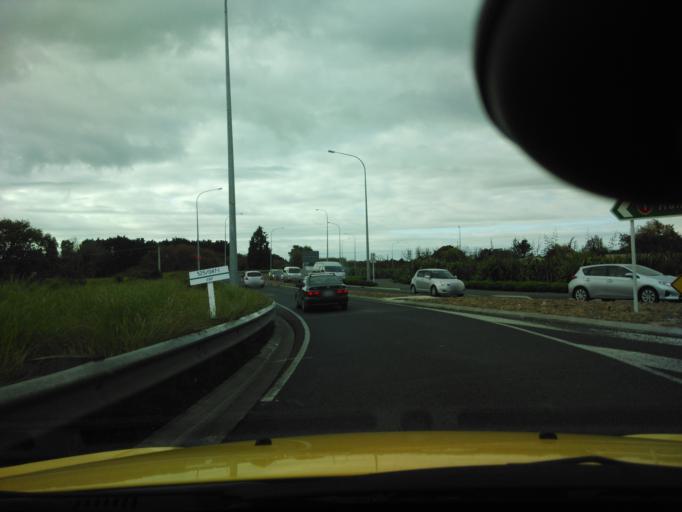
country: NZ
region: Waikato
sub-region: Waikato District
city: Ngaruawahia
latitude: -37.6109
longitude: 175.1915
